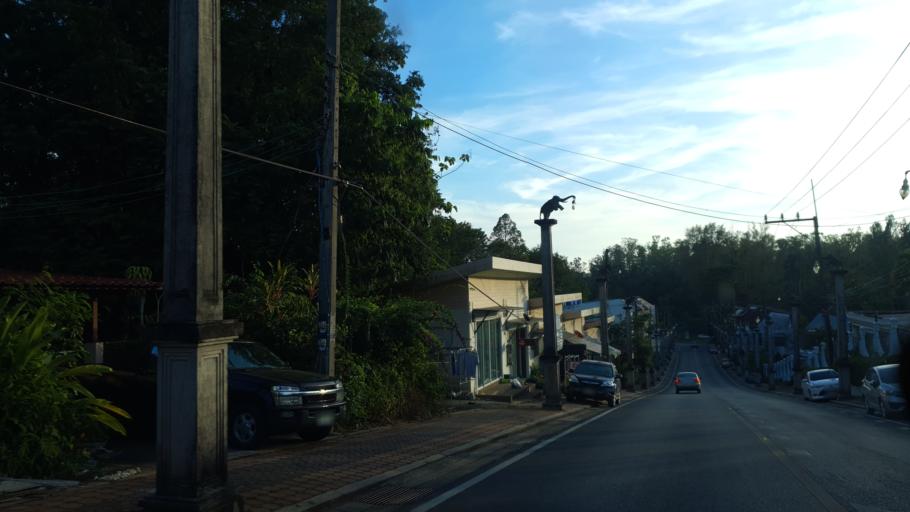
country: TH
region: Krabi
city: Krabi
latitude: 8.0554
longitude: 98.9174
